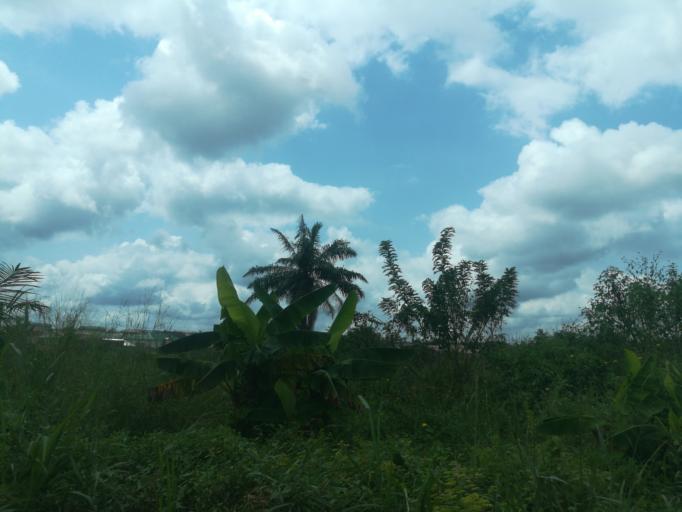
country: NG
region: Oyo
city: Ibadan
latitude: 7.3679
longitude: 3.8258
